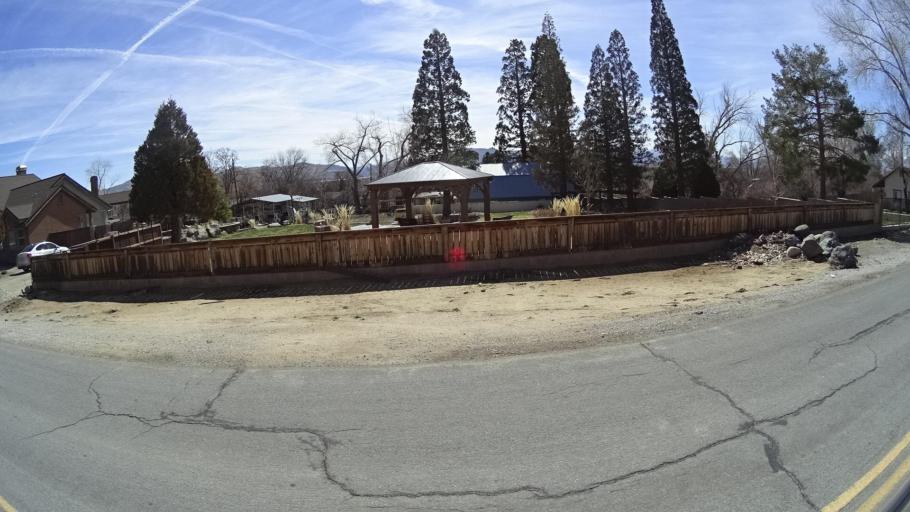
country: US
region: Nevada
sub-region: Washoe County
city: Sparks
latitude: 39.5623
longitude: -119.7557
